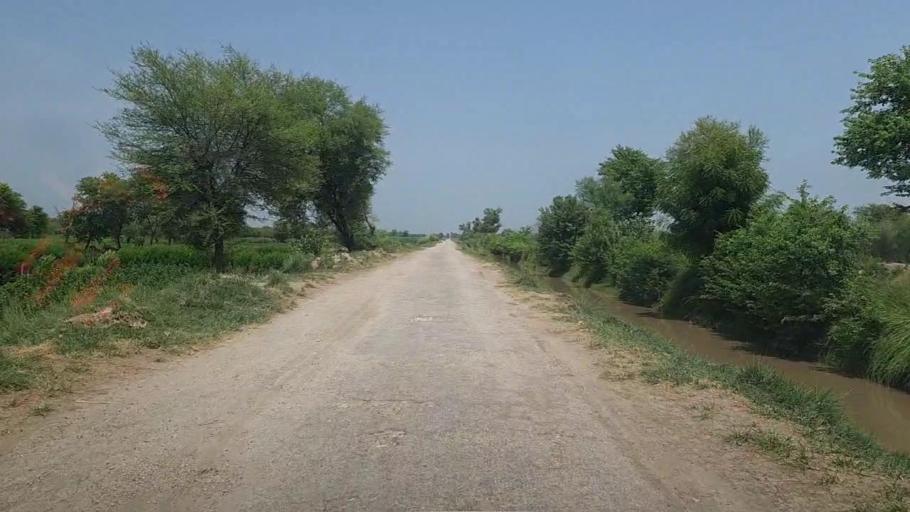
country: PK
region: Sindh
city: Karaundi
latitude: 26.8770
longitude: 68.3359
